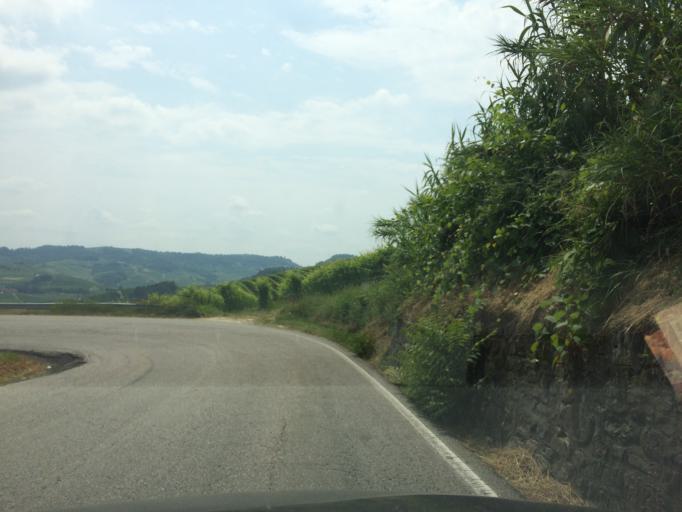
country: IT
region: Piedmont
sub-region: Provincia di Cuneo
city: Barolo
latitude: 44.6154
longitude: 7.9371
